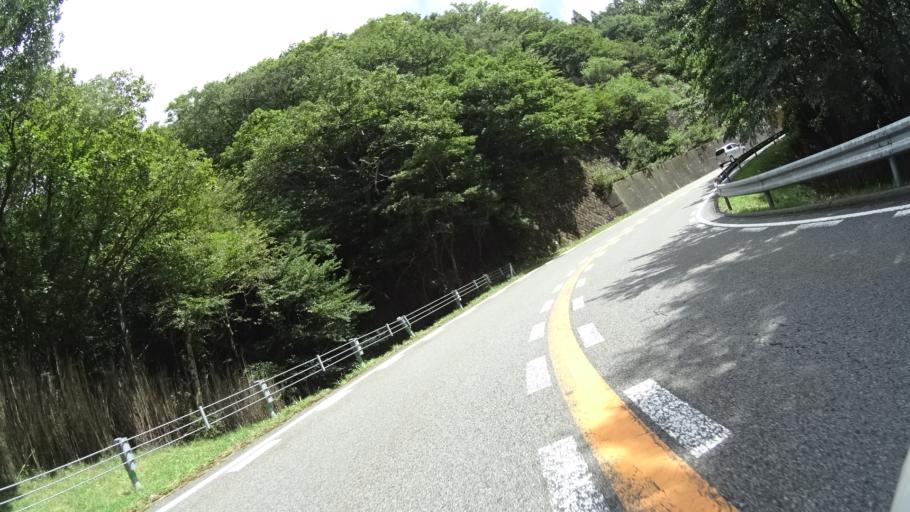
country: JP
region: Kumamoto
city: Aso
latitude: 33.0876
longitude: 131.1940
